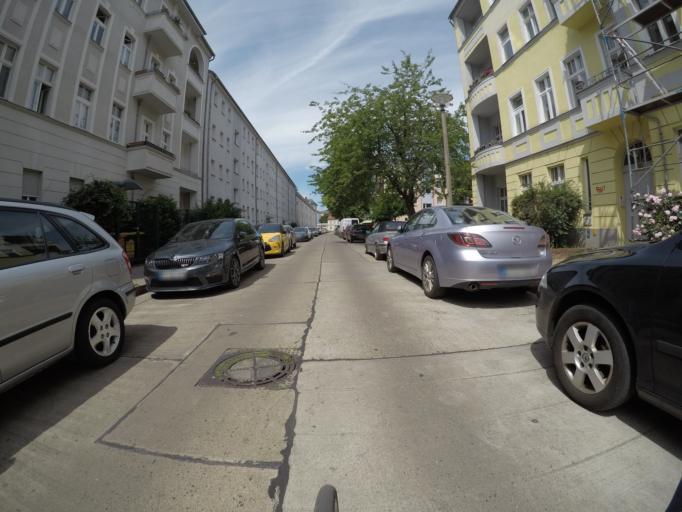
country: DE
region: Berlin
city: Adlershof
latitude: 52.4387
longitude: 13.5549
